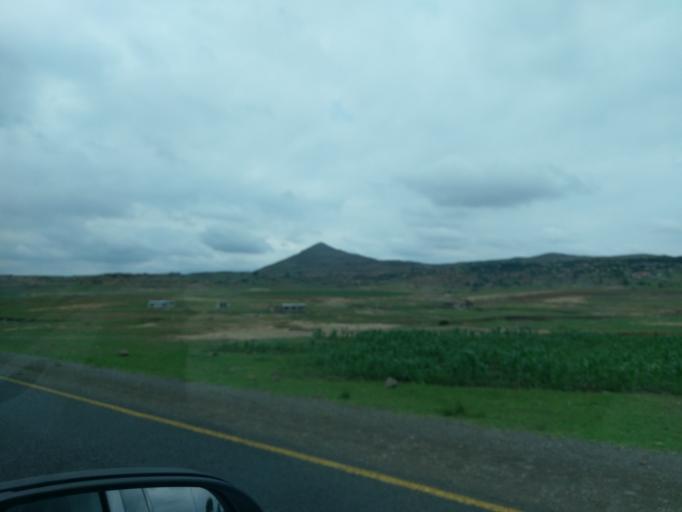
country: LS
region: Mafeteng
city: Mafeteng
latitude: -29.8848
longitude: 27.2477
